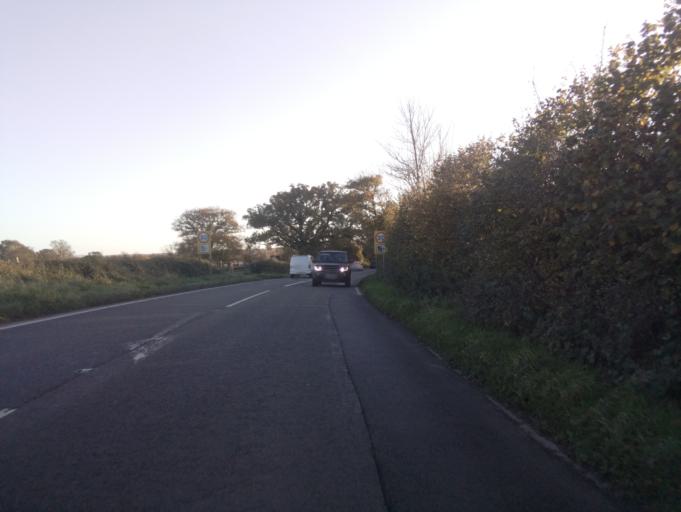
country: GB
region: England
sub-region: Somerset
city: Wincanton
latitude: 51.0427
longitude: -2.4333
